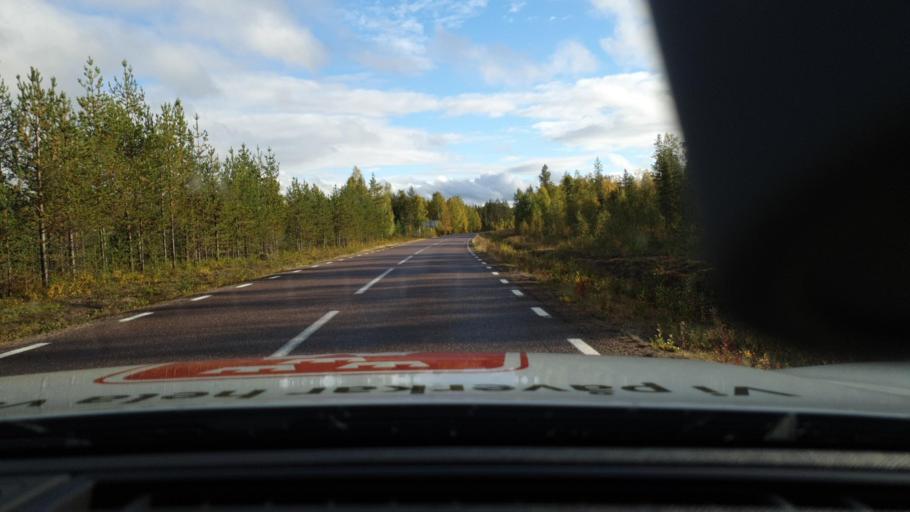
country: SE
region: Norrbotten
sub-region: Overkalix Kommun
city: OEverkalix
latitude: 66.9090
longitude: 22.7747
